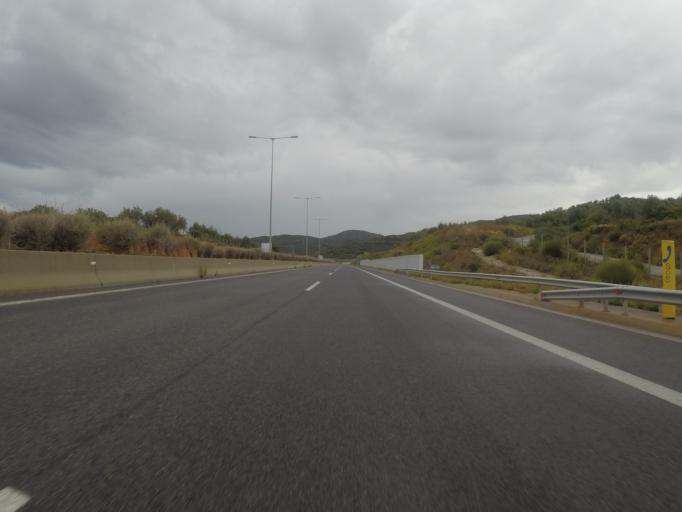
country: GR
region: Peloponnese
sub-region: Nomos Messinias
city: Meligalas
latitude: 37.2545
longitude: 22.0239
